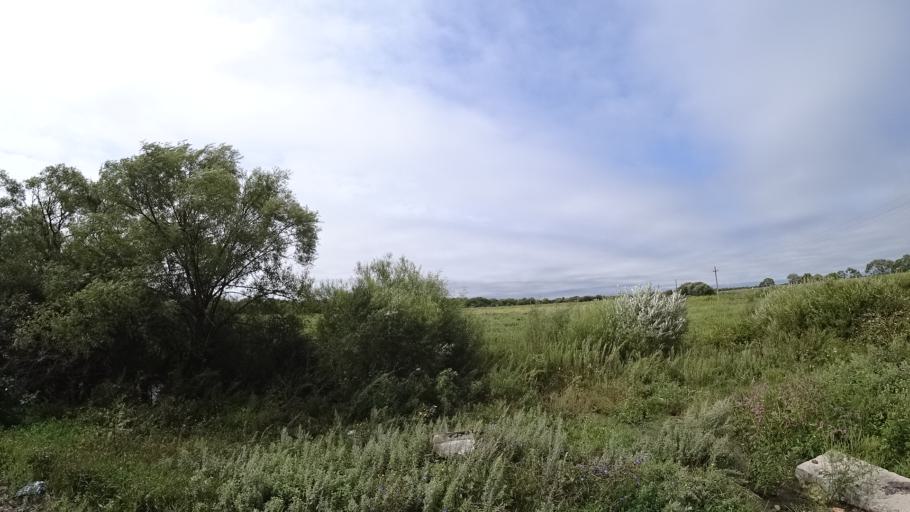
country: RU
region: Primorskiy
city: Monastyrishche
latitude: 44.1765
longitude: 132.4854
